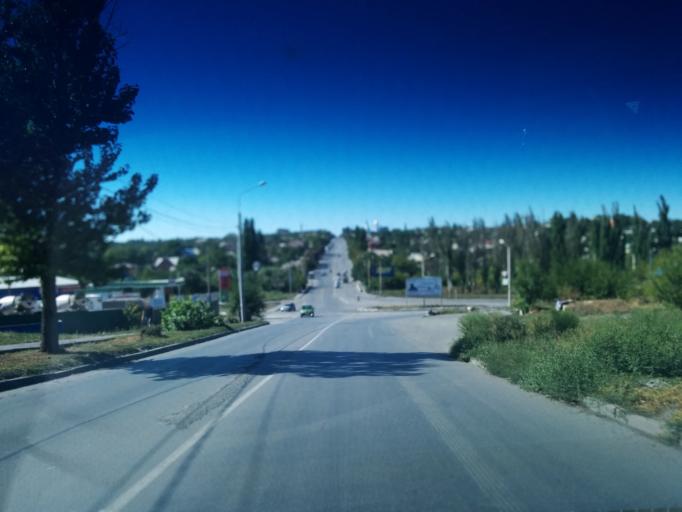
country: RU
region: Rostov
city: Shakhty
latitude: 47.6973
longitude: 40.2394
